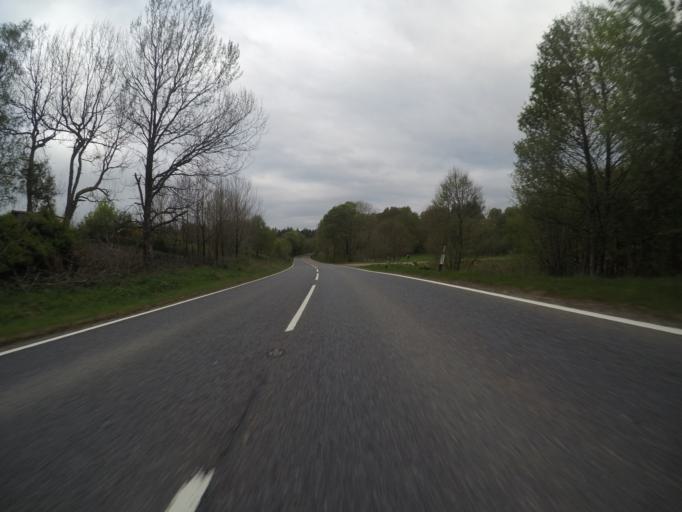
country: GB
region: Scotland
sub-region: Highland
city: Spean Bridge
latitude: 56.8909
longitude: -4.8730
